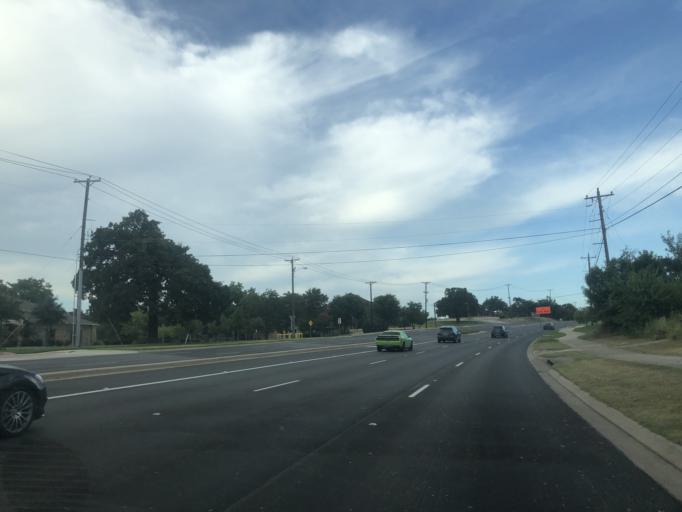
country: US
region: Texas
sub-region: Tarrant County
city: Southlake
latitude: 32.9361
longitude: -97.1884
